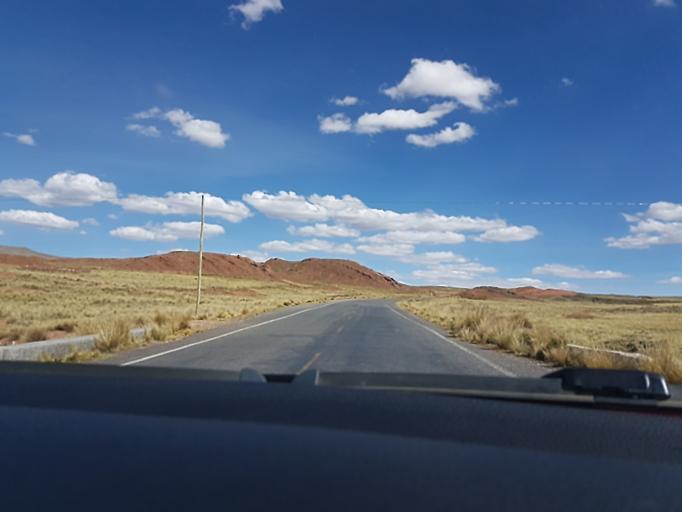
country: BO
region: La Paz
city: Tiahuanaco
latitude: -17.0023
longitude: -68.4263
